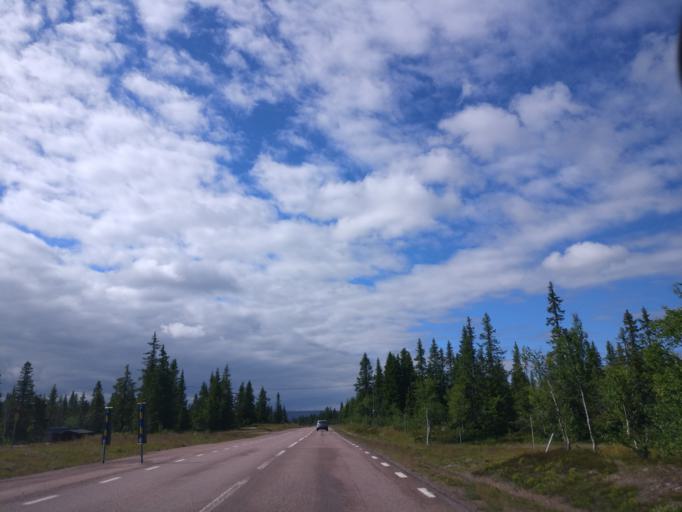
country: SE
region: Dalarna
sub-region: Malung-Saelens kommun
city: Malung
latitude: 61.1636
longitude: 13.1048
